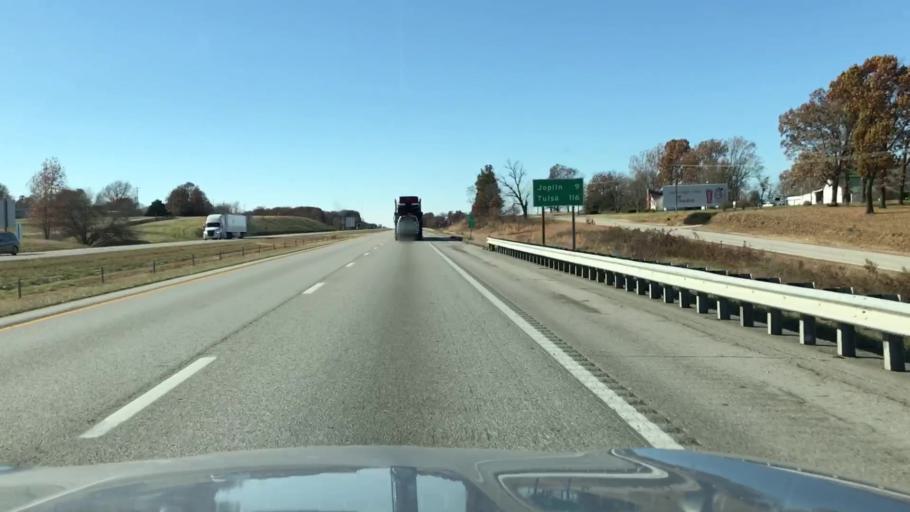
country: US
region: Missouri
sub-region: Jasper County
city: Duenweg
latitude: 37.0822
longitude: -94.3278
